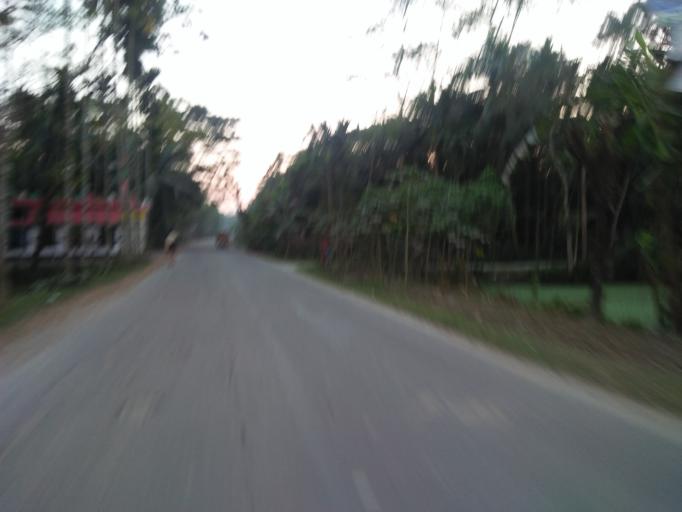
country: BD
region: Barisal
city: Bhola
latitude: 22.7558
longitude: 90.6367
